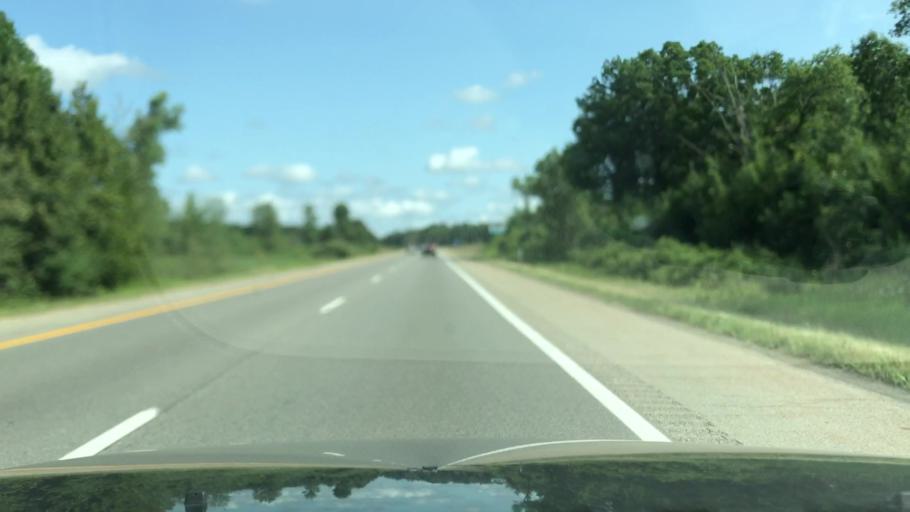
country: US
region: Michigan
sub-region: Kent County
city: Cedar Springs
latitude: 43.2717
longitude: -85.5416
